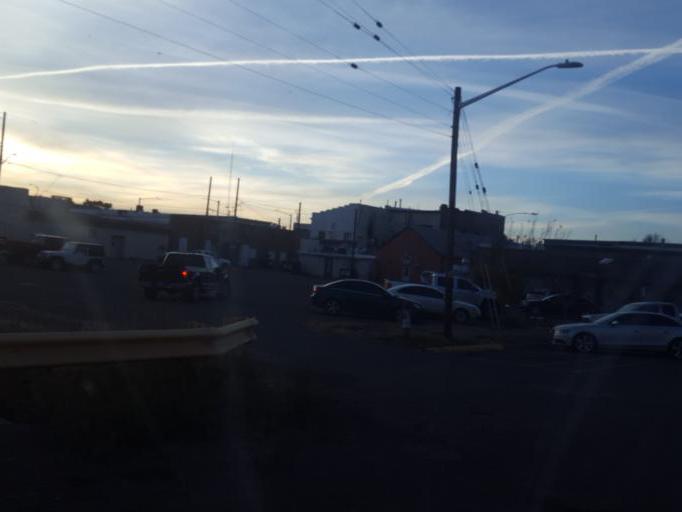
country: US
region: Colorado
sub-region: Rio Grande County
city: Monte Vista
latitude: 37.5814
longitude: -106.1482
